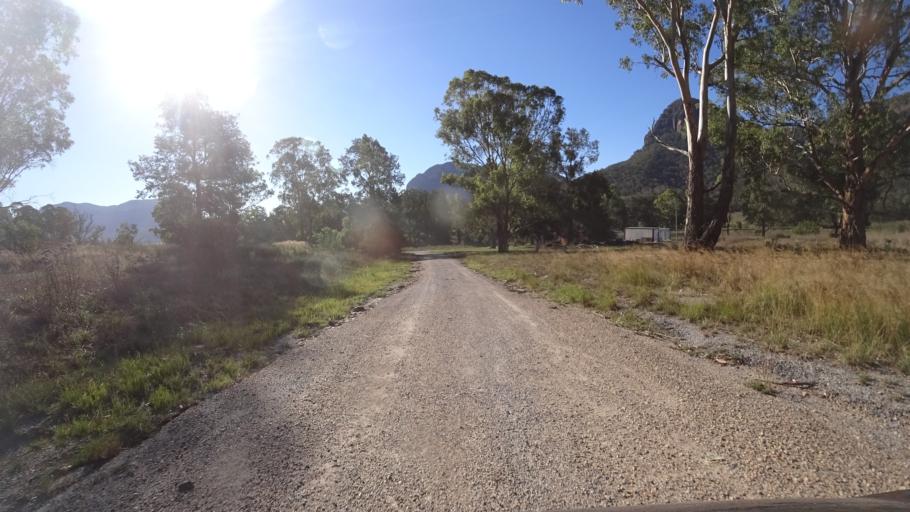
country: AU
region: New South Wales
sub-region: Lithgow
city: Portland
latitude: -33.1235
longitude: 150.2807
